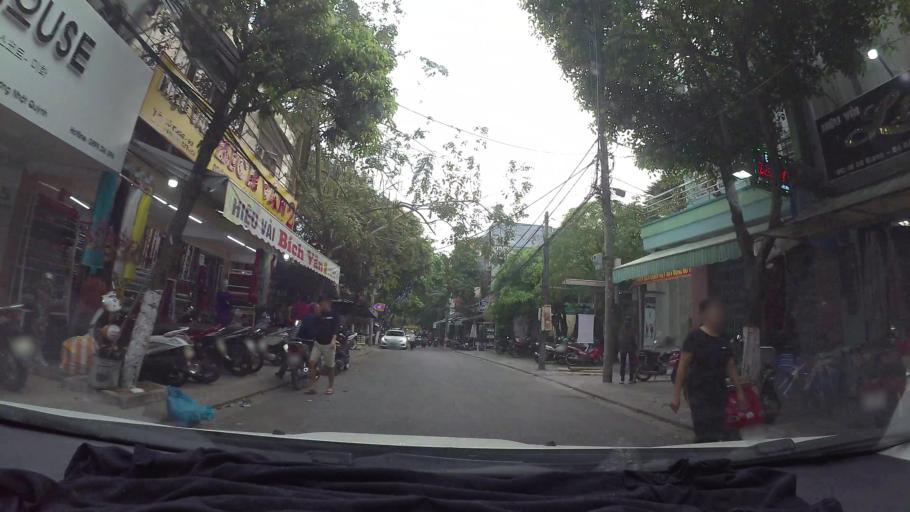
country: VN
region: Da Nang
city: Da Nang
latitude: 16.0622
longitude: 108.2218
